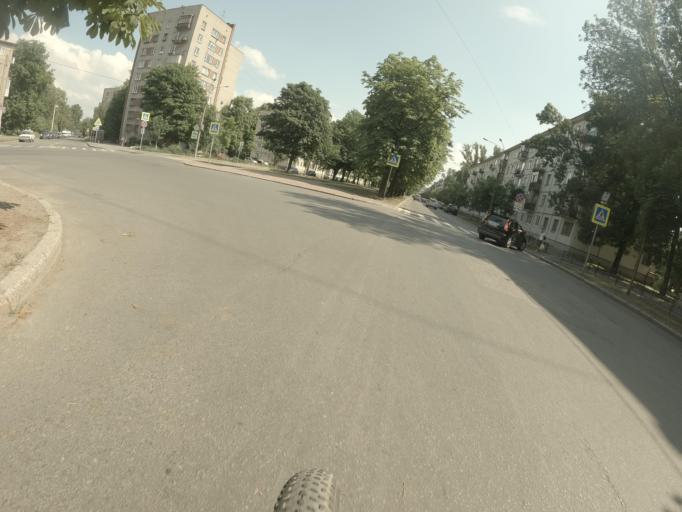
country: RU
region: St.-Petersburg
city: Centralniy
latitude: 59.9252
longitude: 30.4230
